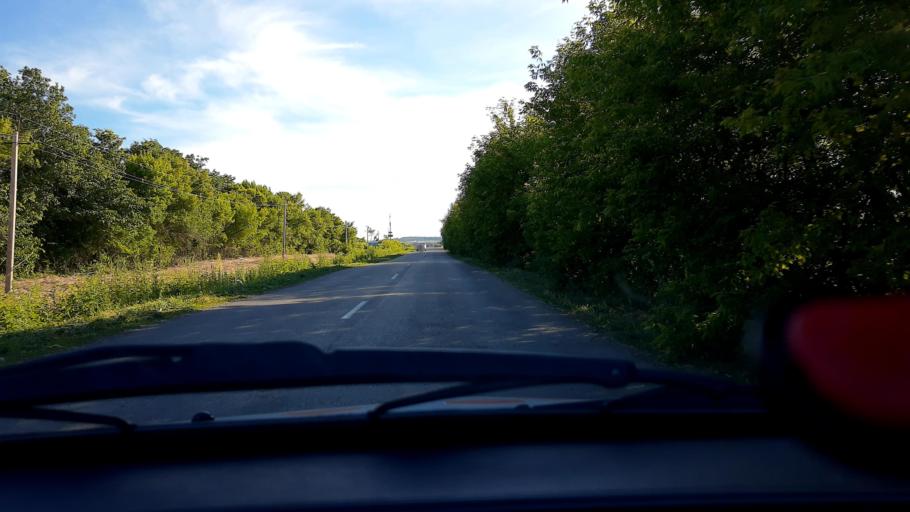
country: RU
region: Bashkortostan
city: Kabakovo
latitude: 54.5088
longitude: 55.9343
